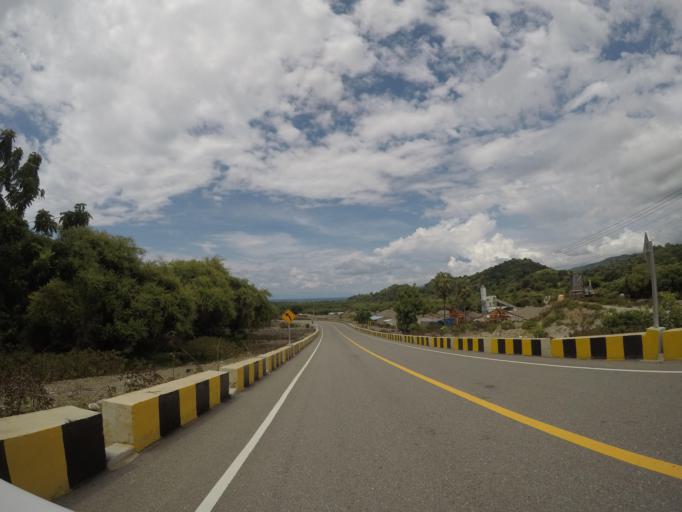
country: TL
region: Bobonaro
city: Maliana
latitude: -8.8430
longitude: 125.0603
